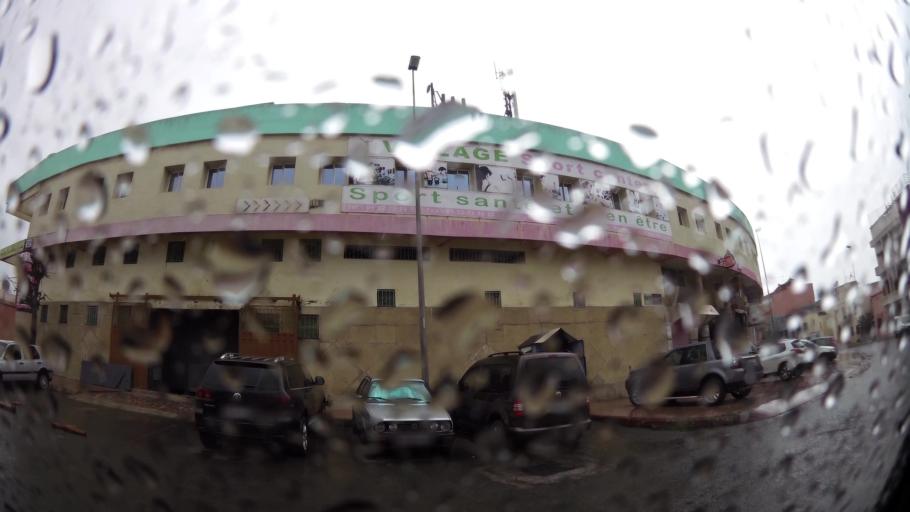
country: MA
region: Grand Casablanca
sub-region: Mediouna
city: Tit Mellil
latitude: 33.6201
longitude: -7.4807
